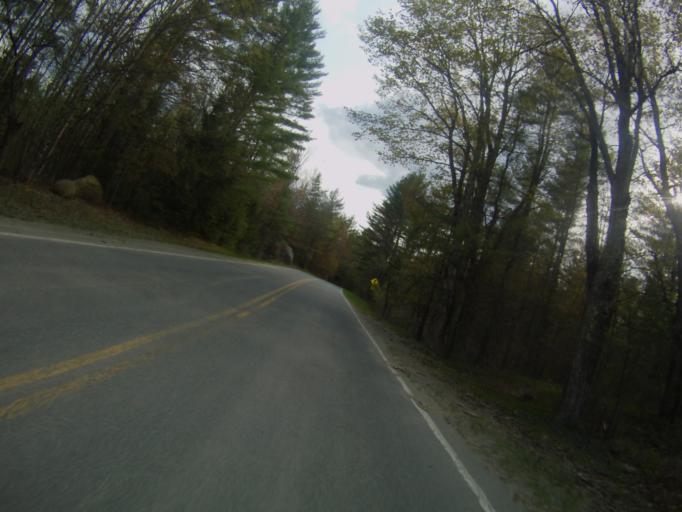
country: US
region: New York
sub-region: Warren County
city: Warrensburg
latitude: 43.8361
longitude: -73.8941
